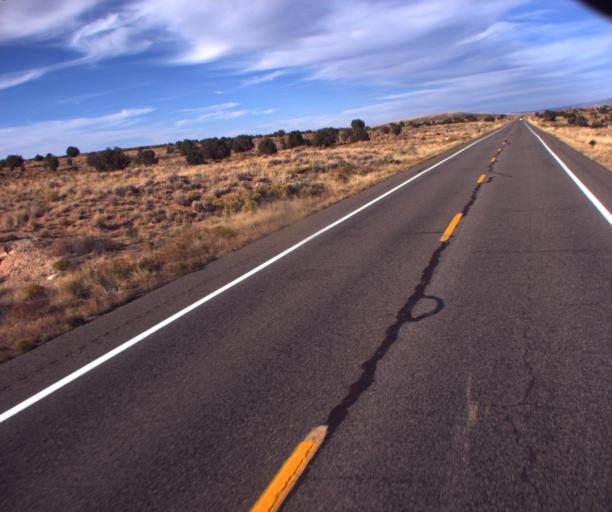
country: US
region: Colorado
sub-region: Montezuma County
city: Towaoc
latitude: 36.9720
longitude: -109.0612
